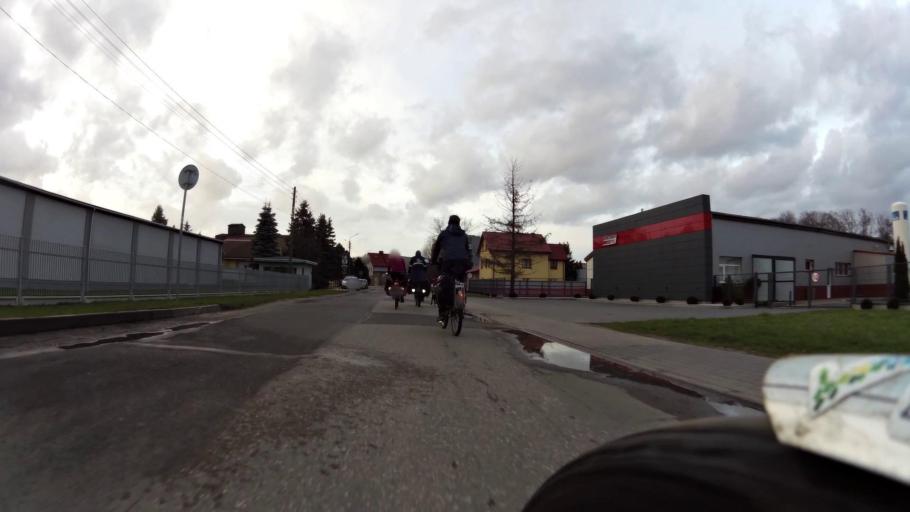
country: PL
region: West Pomeranian Voivodeship
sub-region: Powiat kamienski
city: Kamien Pomorski
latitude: 53.9626
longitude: 14.7686
